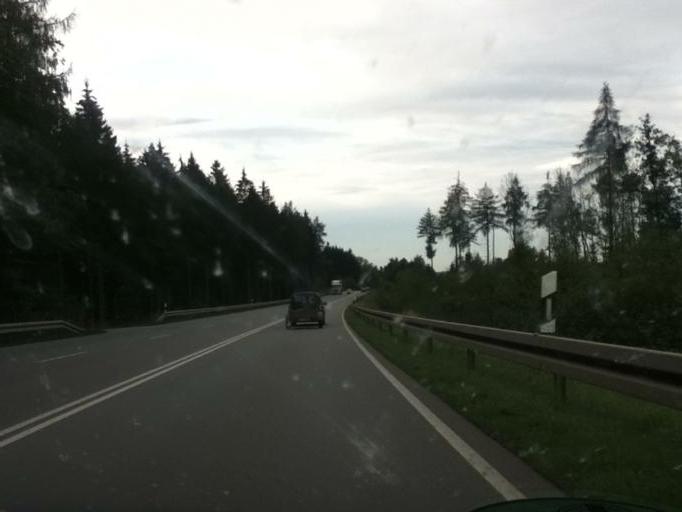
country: DE
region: Saxony
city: Hartenstein
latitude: 50.6494
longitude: 12.7007
